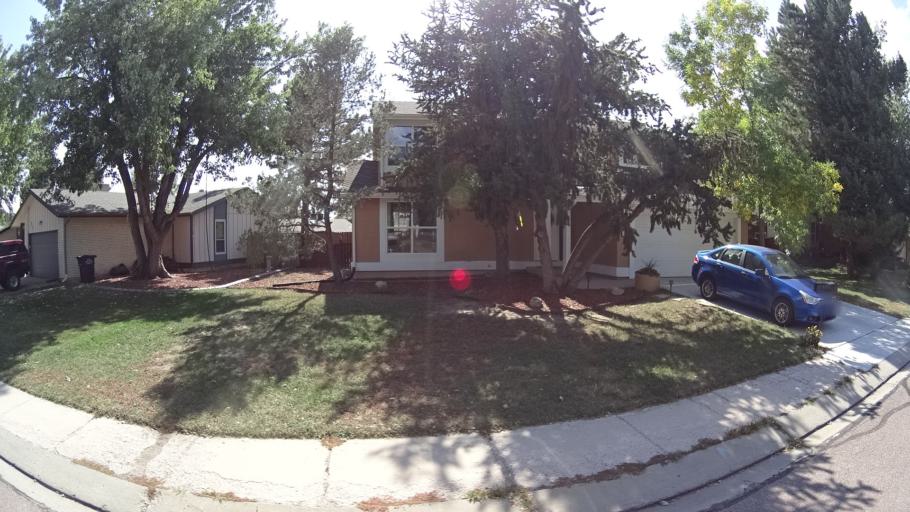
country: US
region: Colorado
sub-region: El Paso County
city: Cimarron Hills
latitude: 38.8712
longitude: -104.7539
